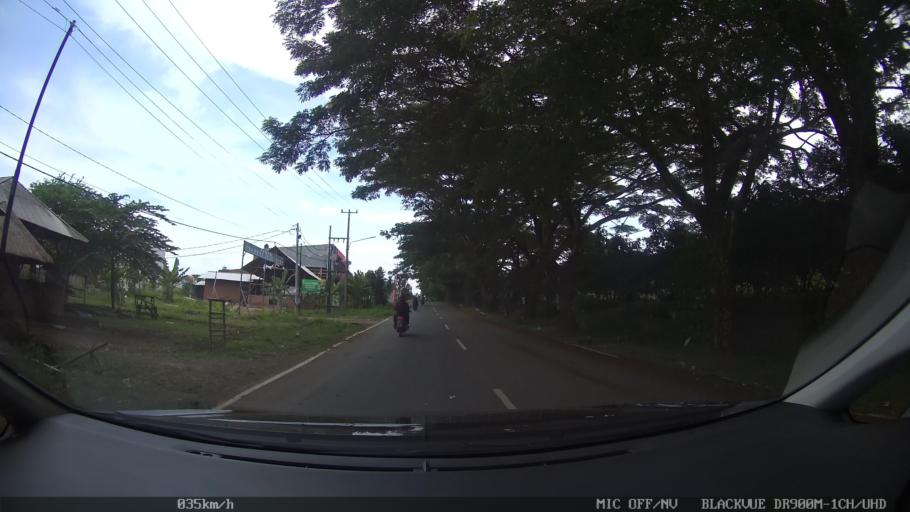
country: ID
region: Lampung
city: Bandarlampung
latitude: -5.4114
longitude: 105.1926
